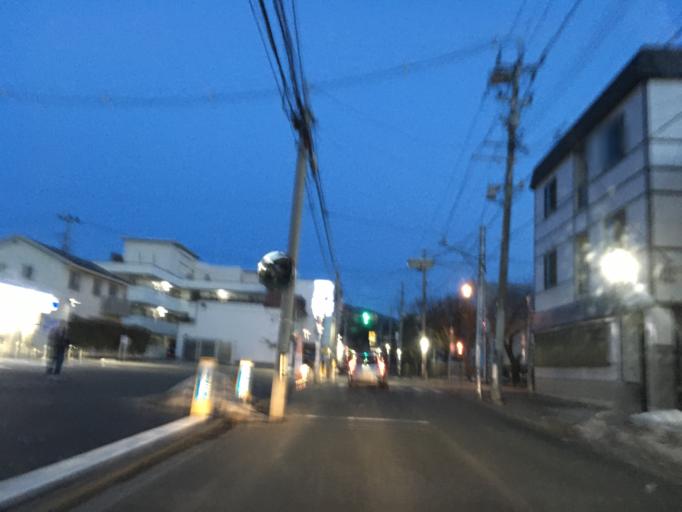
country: JP
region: Iwate
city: Morioka-shi
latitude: 39.7043
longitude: 141.1599
